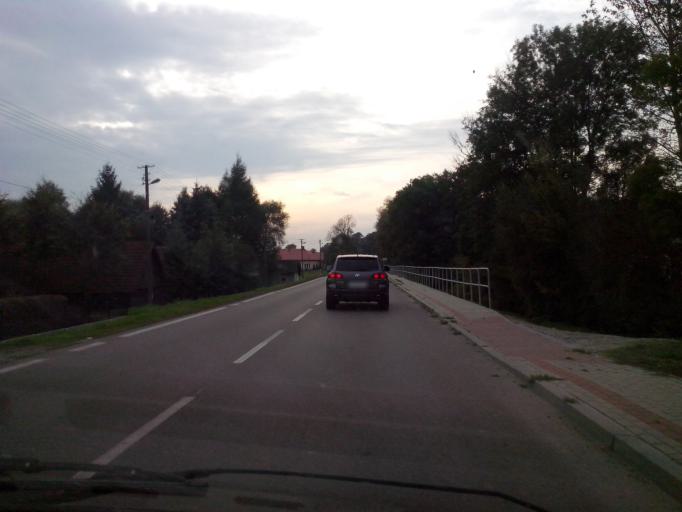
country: PL
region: Subcarpathian Voivodeship
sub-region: Powiat rzeszowski
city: Dynow
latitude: 49.8373
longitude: 22.2609
